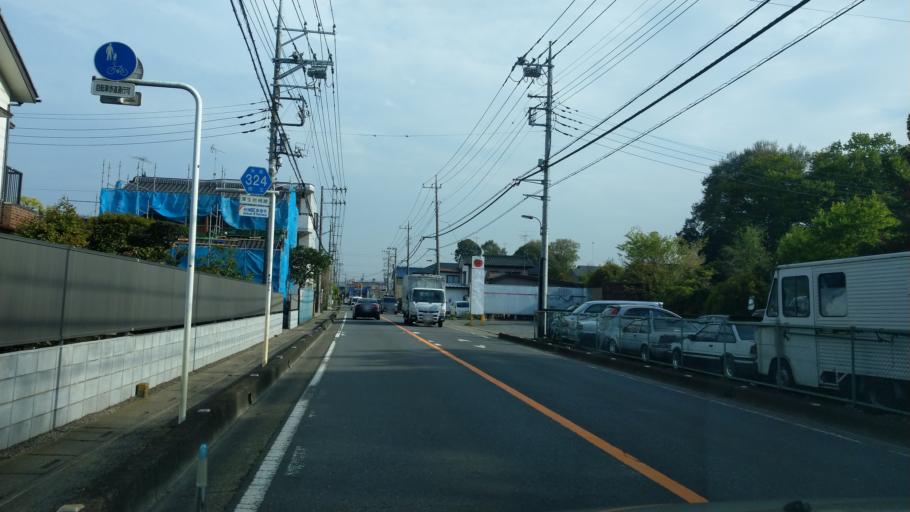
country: JP
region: Saitama
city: Iwatsuki
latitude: 35.9340
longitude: 139.7113
